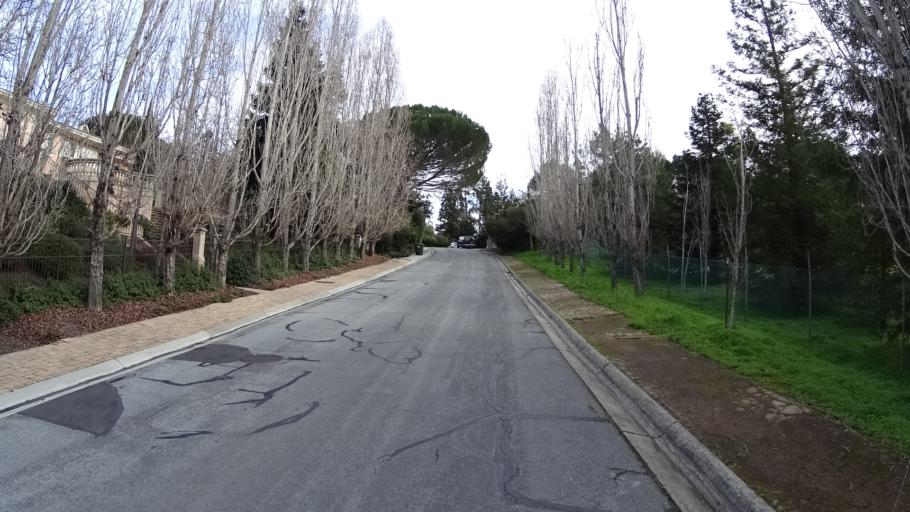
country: US
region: California
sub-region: San Mateo County
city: Hillsborough
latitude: 37.5595
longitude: -122.3589
